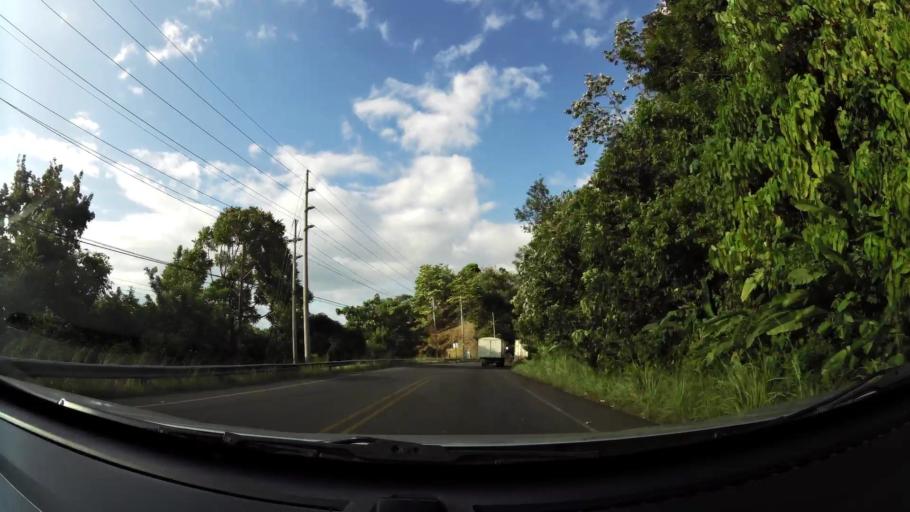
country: CR
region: Puntarenas
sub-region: Canton de Garabito
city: Jaco
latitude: 9.7488
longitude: -84.6300
